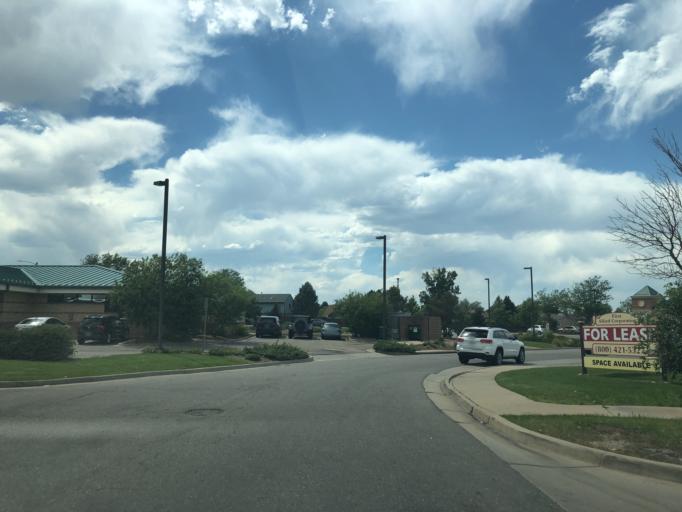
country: US
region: Colorado
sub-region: Arapahoe County
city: Dove Valley
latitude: 39.6191
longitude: -104.7717
